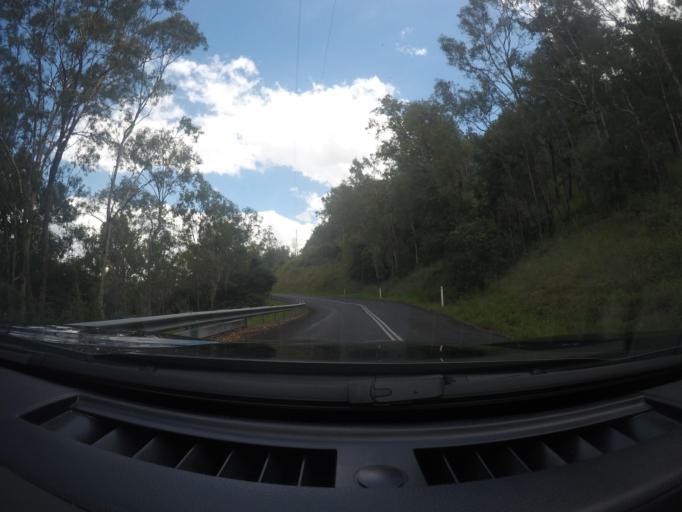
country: AU
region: Queensland
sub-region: Moreton Bay
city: Woodford
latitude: -27.0949
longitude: 152.5620
